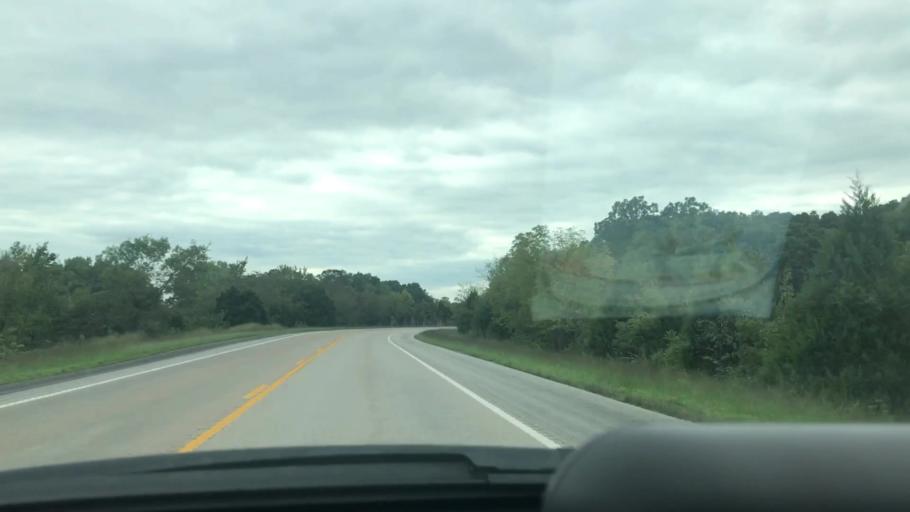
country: US
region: Missouri
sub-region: Benton County
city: Warsaw
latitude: 38.2115
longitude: -93.3416
